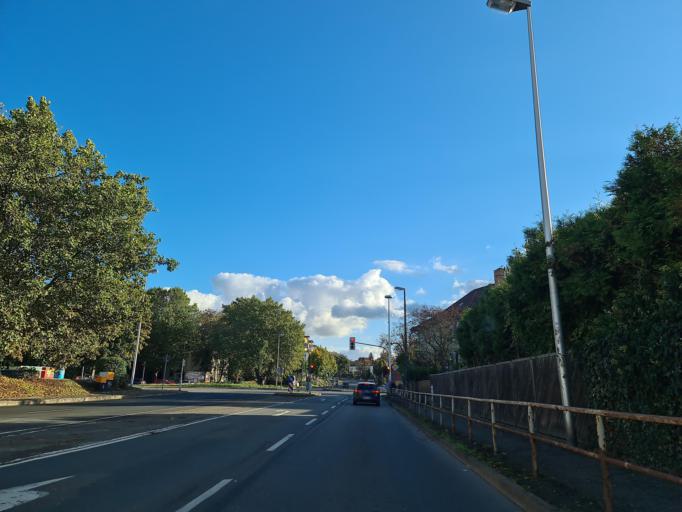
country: DE
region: Thuringia
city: Gera
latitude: 50.8889
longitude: 12.0905
